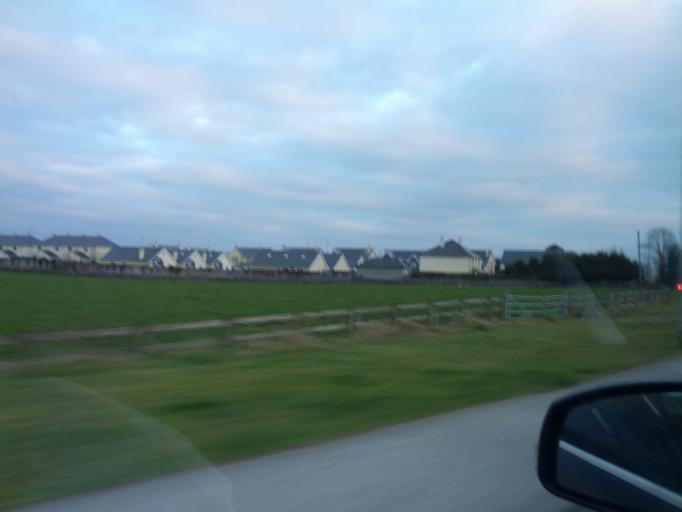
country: IE
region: Connaught
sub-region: County Galway
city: Athenry
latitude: 53.3093
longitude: -8.7543
